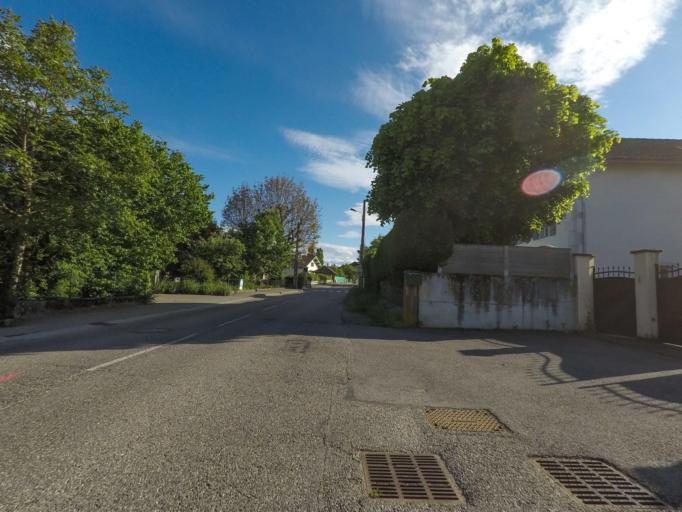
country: FR
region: Rhone-Alpes
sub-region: Departement de l'Ain
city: Saint-Genis-Pouilly
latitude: 46.2533
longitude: 6.0348
